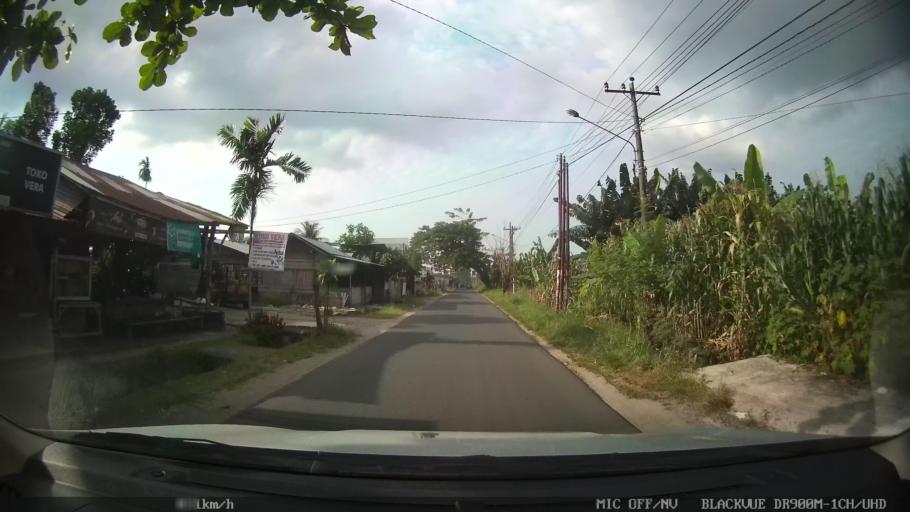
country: ID
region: North Sumatra
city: Sunggal
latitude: 3.5363
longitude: 98.6053
